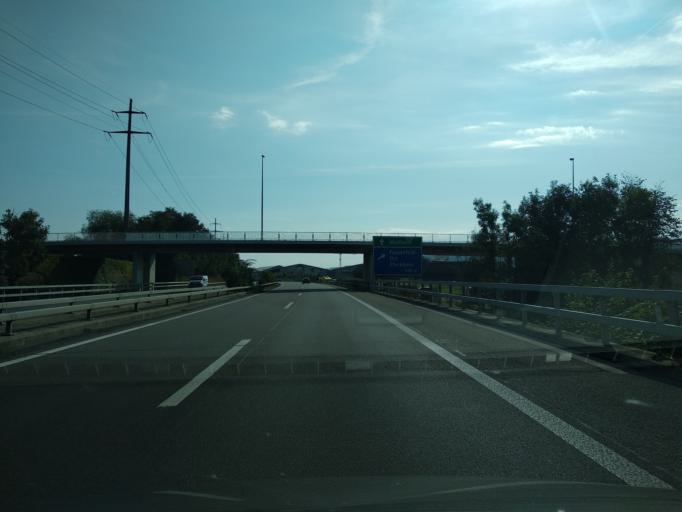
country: CH
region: Thurgau
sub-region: Frauenfeld District
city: Frauenfeld
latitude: 47.5659
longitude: 8.8951
